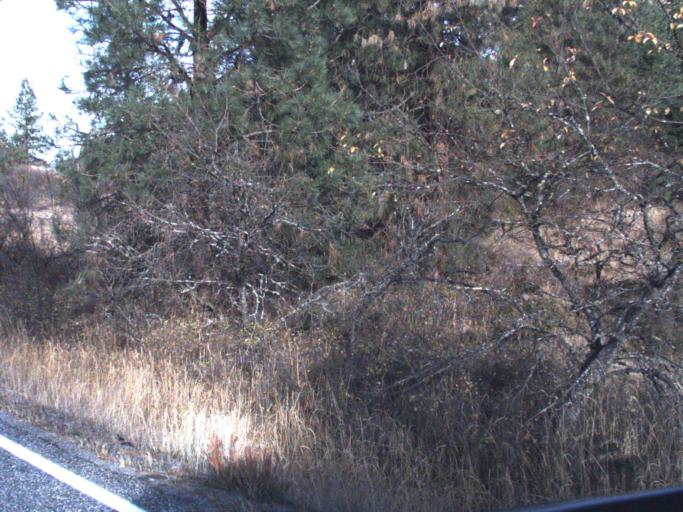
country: CA
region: British Columbia
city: Rossland
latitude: 48.8598
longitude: -117.8776
